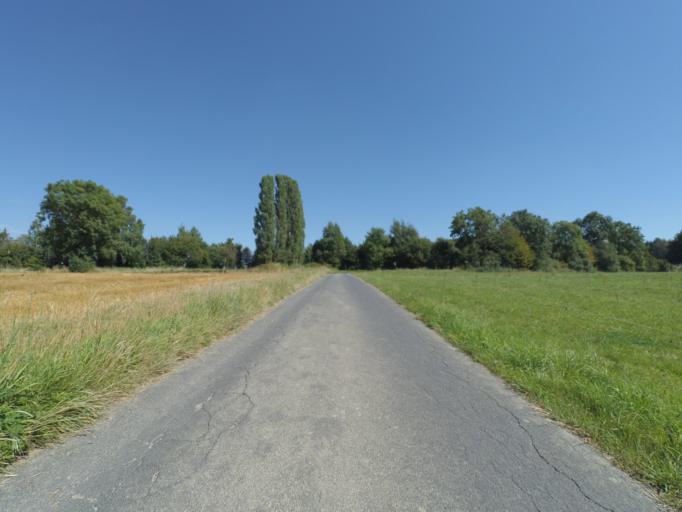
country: DE
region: Rheinland-Pfalz
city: Alflen
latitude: 50.1837
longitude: 7.0544
